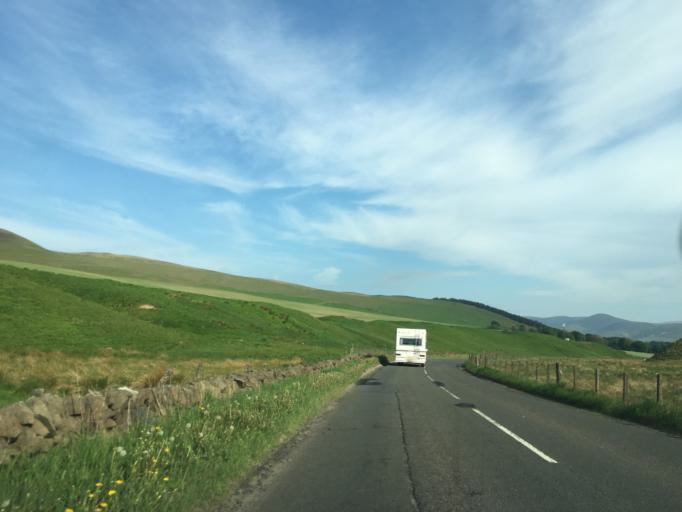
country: GB
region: Scotland
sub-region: South Lanarkshire
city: Biggar
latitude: 55.6352
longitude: -3.4237
